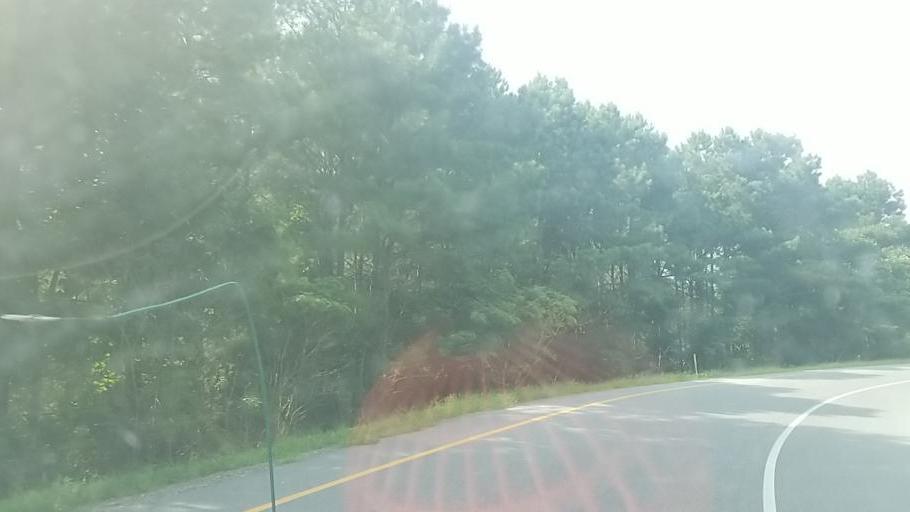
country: US
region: Maryland
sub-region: Worcester County
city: Berlin
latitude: 38.3762
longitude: -75.2080
